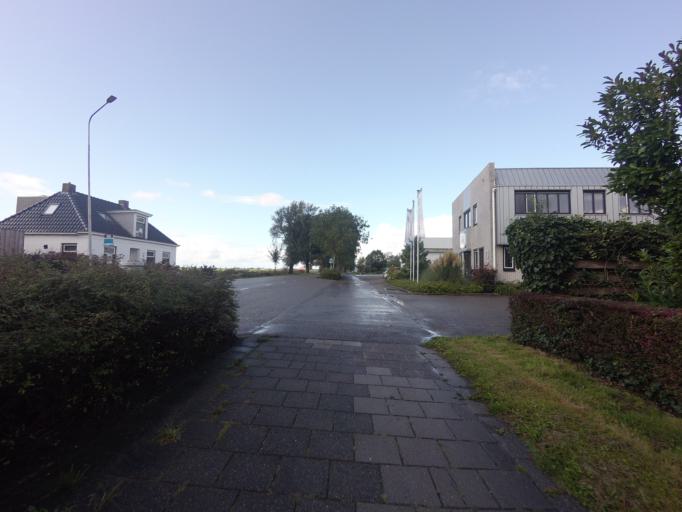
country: NL
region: Friesland
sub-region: Gemeente Boarnsterhim
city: Warten
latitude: 53.1494
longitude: 5.8890
